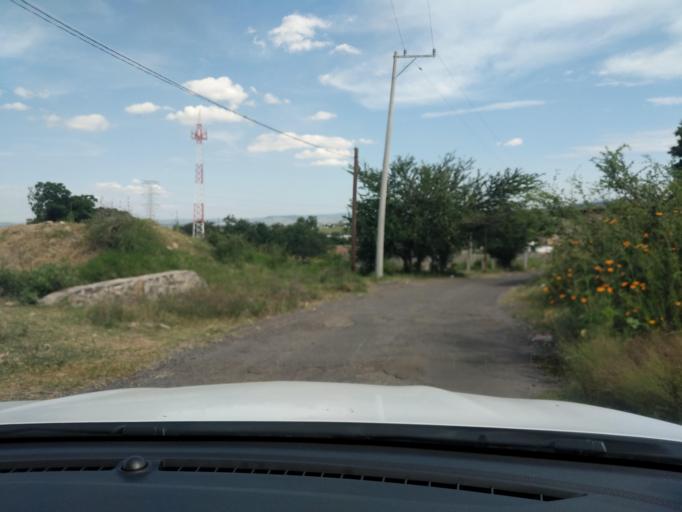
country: MX
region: Jalisco
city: Coyula
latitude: 20.6290
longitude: -103.2171
